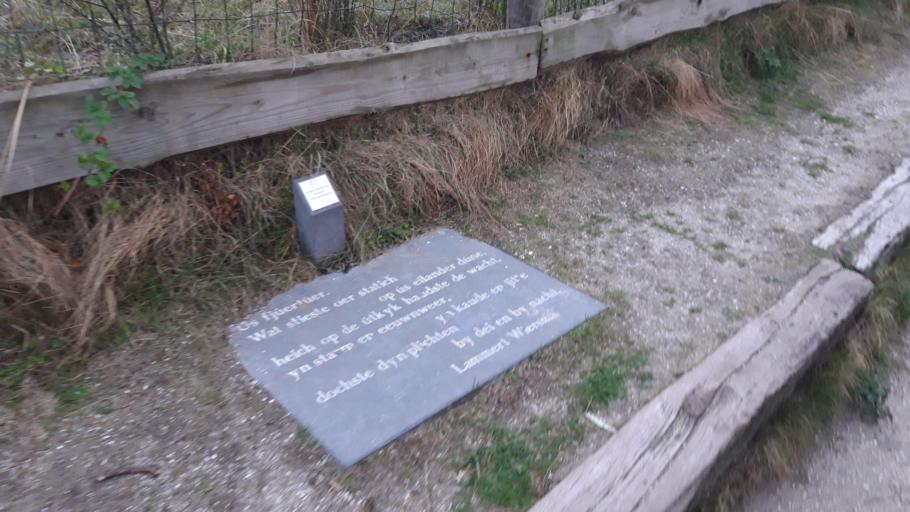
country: NL
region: Friesland
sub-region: Gemeente Schiermonnikoog
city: Schiermonnikoog
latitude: 53.4868
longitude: 6.1466
